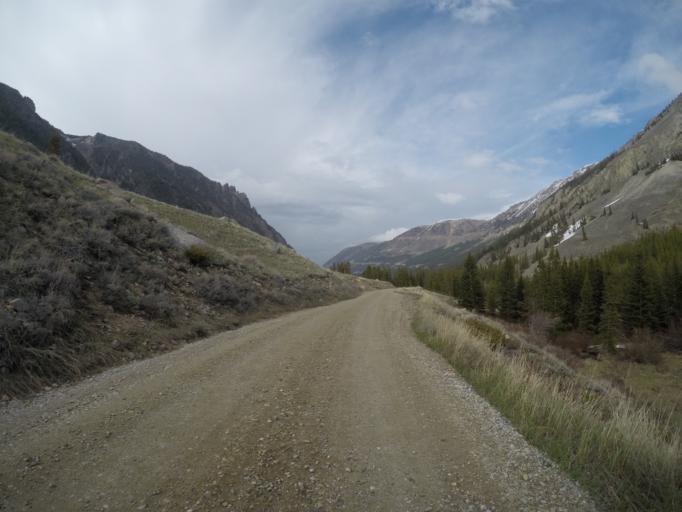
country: US
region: Montana
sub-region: Carbon County
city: Red Lodge
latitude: 45.0219
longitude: -109.4508
